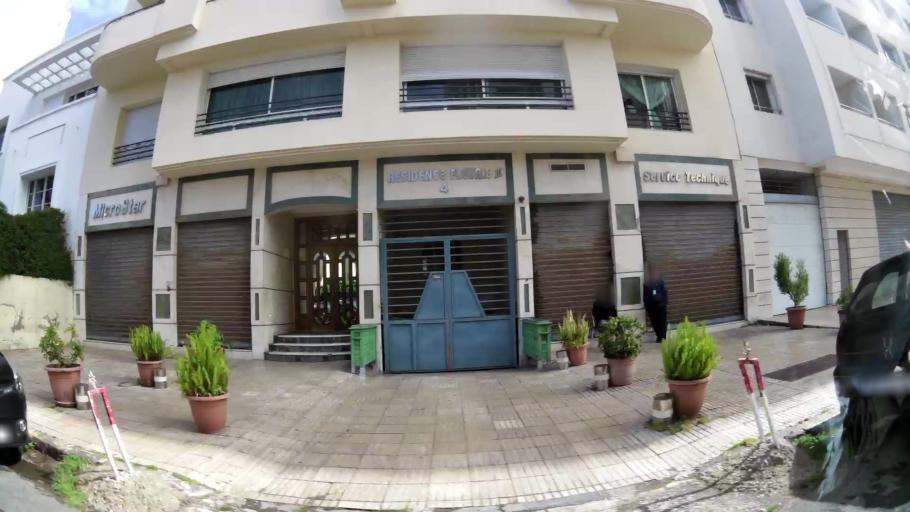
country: MA
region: Grand Casablanca
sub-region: Casablanca
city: Casablanca
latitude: 33.5832
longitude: -7.6281
